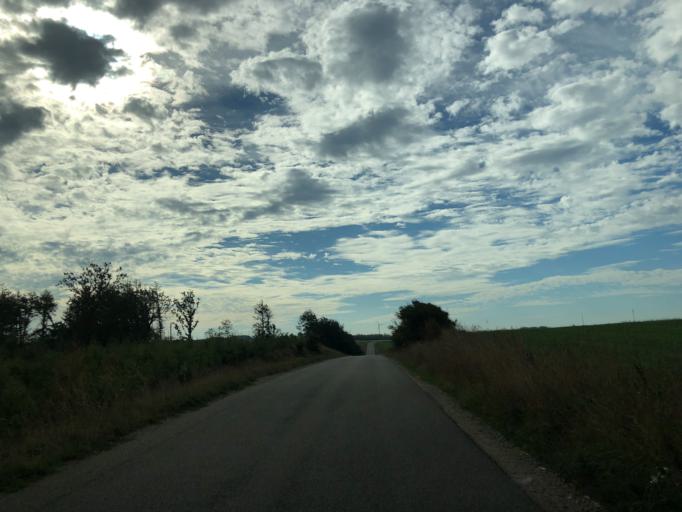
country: DK
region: Central Jutland
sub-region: Ringkobing-Skjern Kommune
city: Skjern
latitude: 56.0998
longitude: 8.4377
